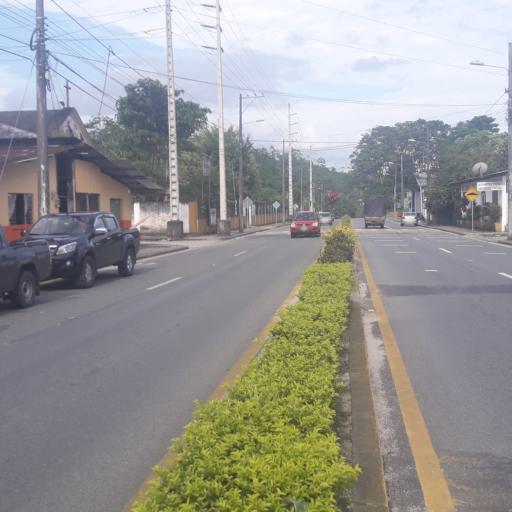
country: EC
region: Napo
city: Tena
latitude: -0.9835
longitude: -77.8105
